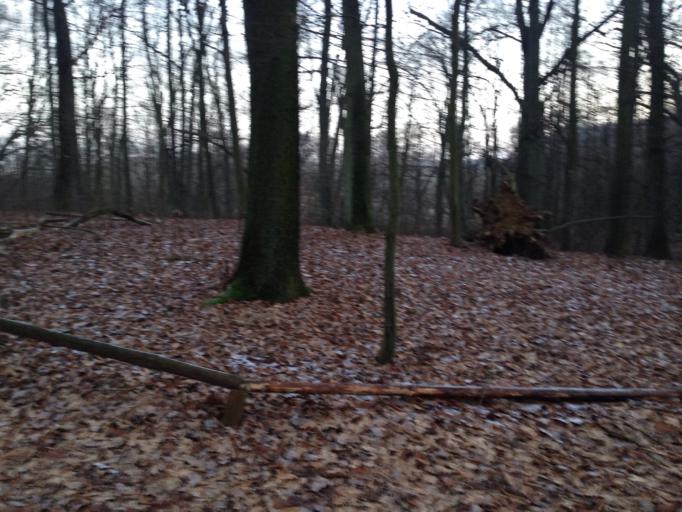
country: PL
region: Greater Poland Voivodeship
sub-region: Powiat poznanski
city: Suchy Las
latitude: 52.4898
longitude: 16.8967
